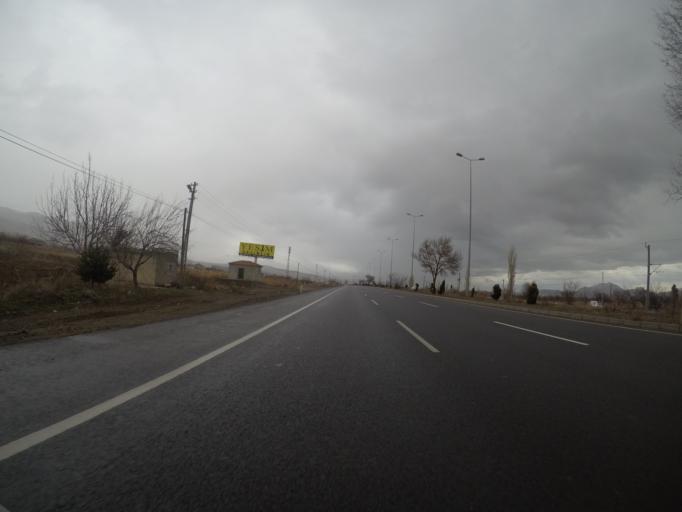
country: TR
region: Kayseri
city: Incesu
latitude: 38.6933
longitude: 35.2453
